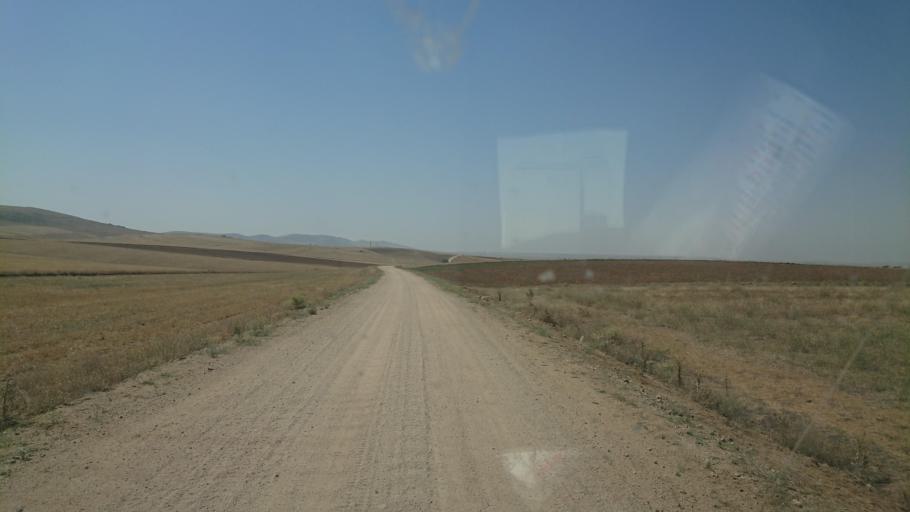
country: TR
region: Aksaray
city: Agacoren
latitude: 38.7976
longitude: 33.9428
